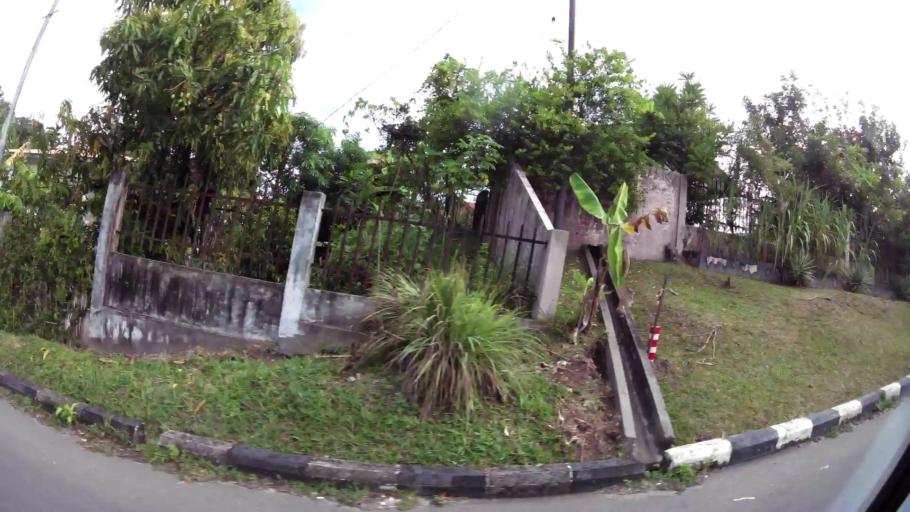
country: BN
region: Brunei and Muara
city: Bandar Seri Begawan
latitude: 4.9000
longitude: 114.8928
